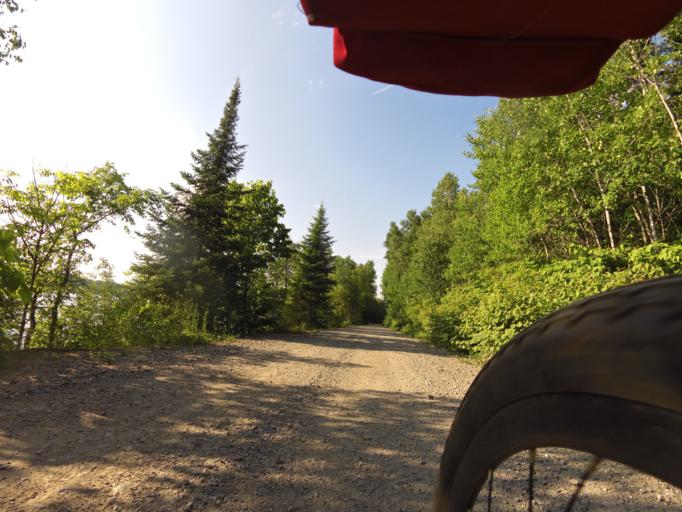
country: CA
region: Quebec
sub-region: Outaouais
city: Maniwaki
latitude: 46.3203
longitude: -76.0064
